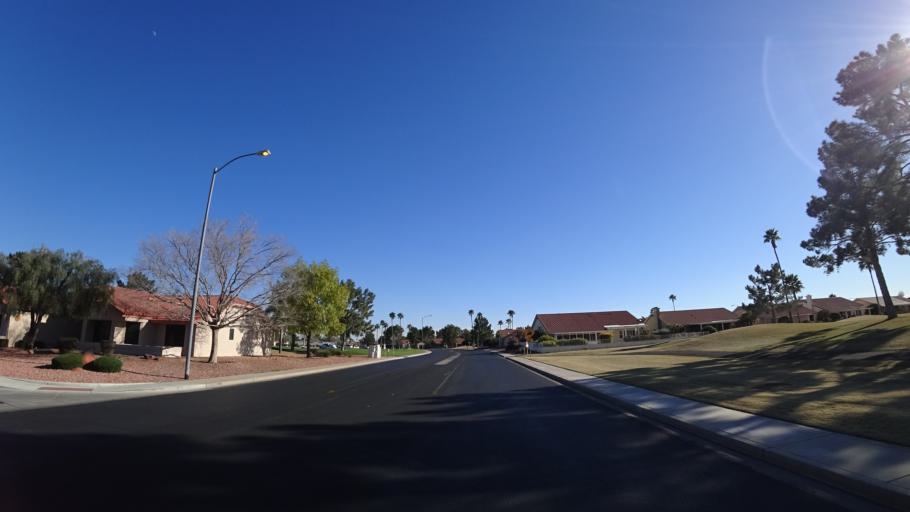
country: US
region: Arizona
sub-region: Maricopa County
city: Sun City West
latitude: 33.6705
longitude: -112.3602
